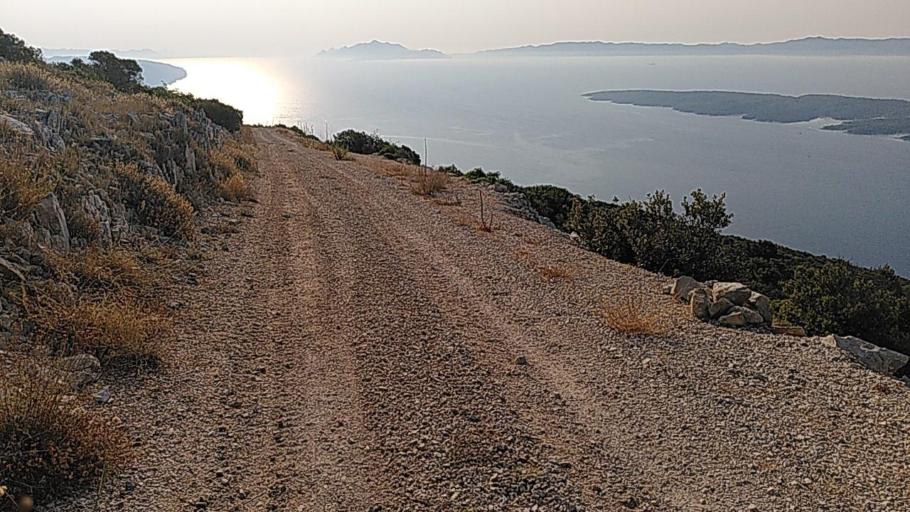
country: HR
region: Splitsko-Dalmatinska
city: Jelsa
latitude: 43.1334
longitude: 16.6631
